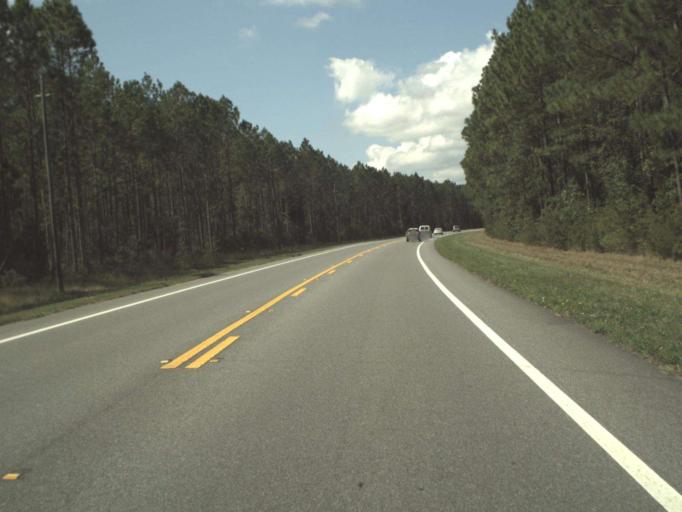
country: US
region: Florida
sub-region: Walton County
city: Freeport
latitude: 30.4805
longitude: -86.0970
